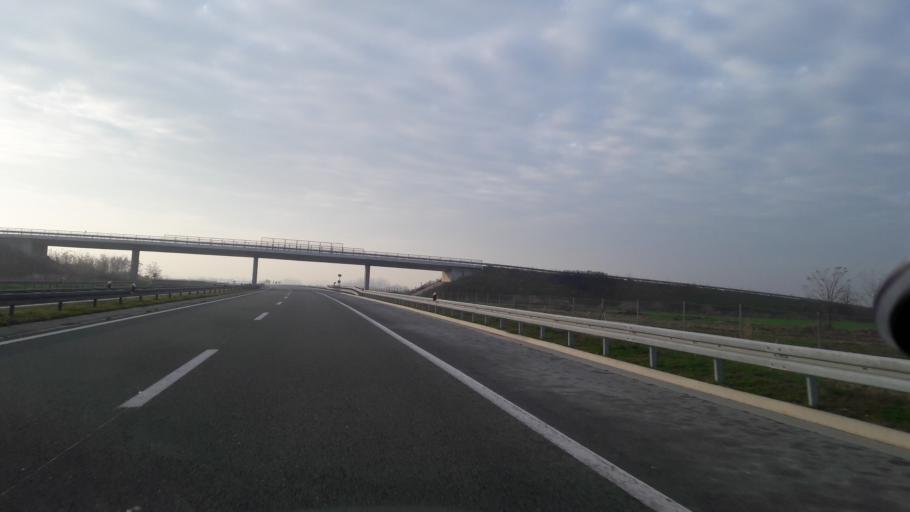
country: HR
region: Osjecko-Baranjska
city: Gorjani
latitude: 45.3798
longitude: 18.3953
